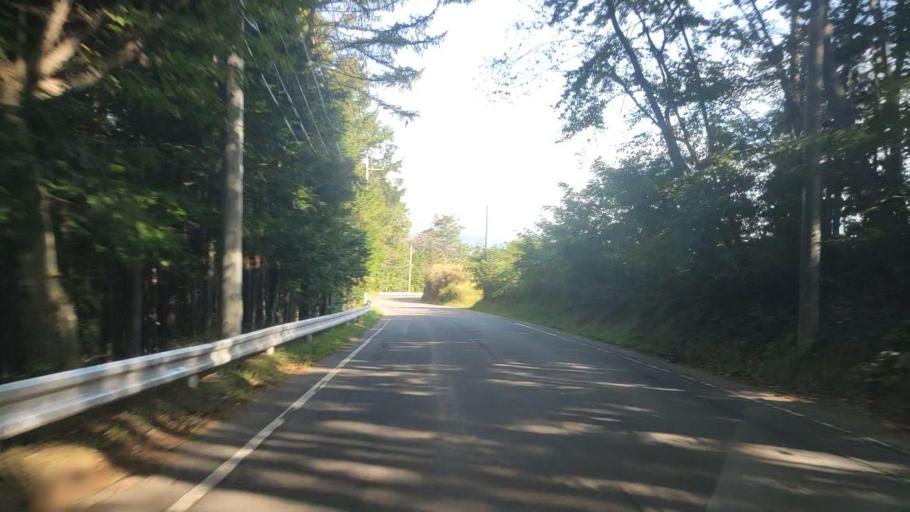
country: JP
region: Nagano
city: Suzaka
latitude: 36.5606
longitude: 138.5581
